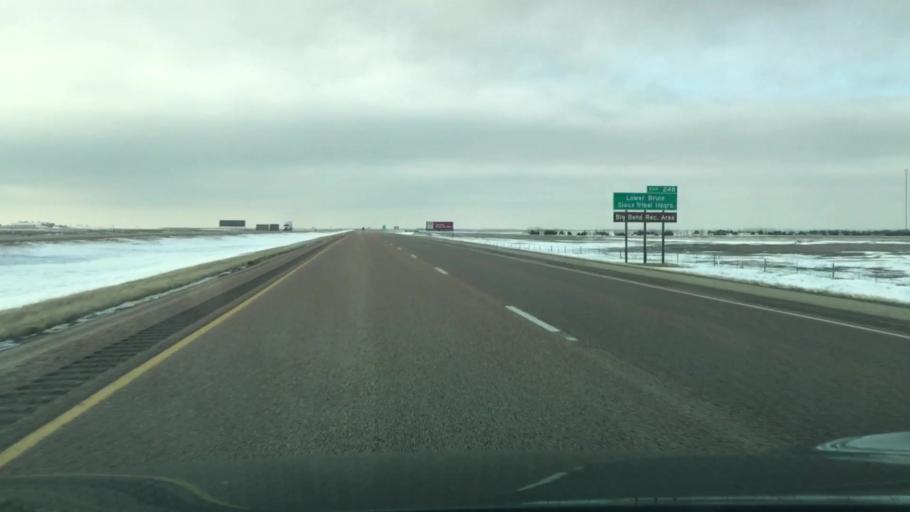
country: US
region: South Dakota
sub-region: Buffalo County
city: Fort Thompson
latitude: 43.8589
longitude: -99.5896
